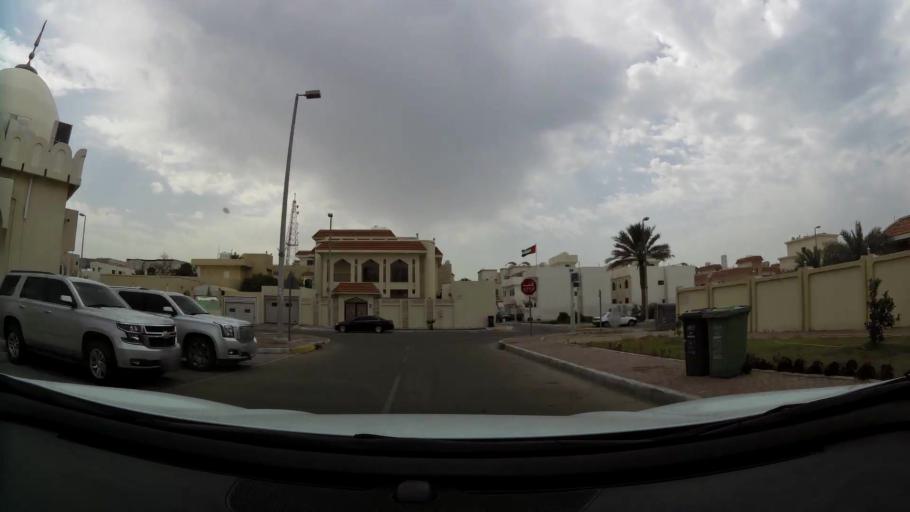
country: AE
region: Abu Dhabi
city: Abu Dhabi
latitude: 24.4632
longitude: 54.3569
